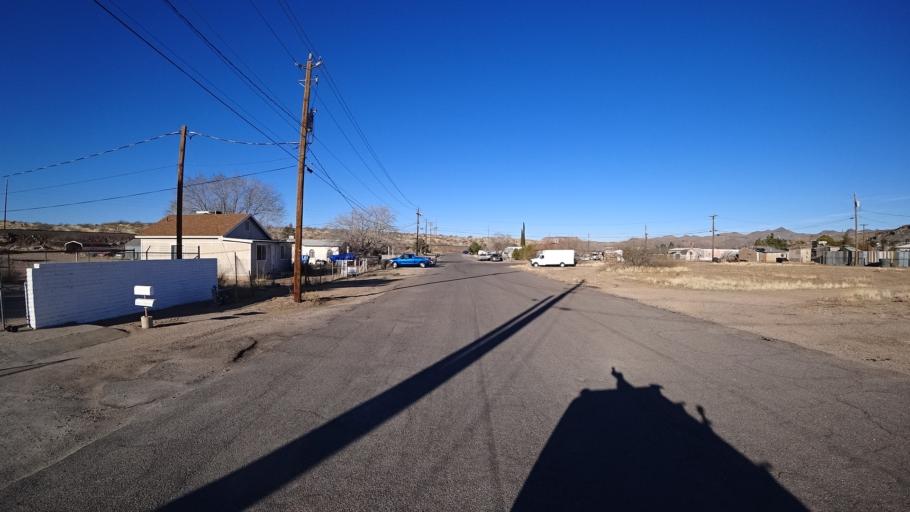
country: US
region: Arizona
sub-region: Mohave County
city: Kingman
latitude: 35.1829
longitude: -114.0424
